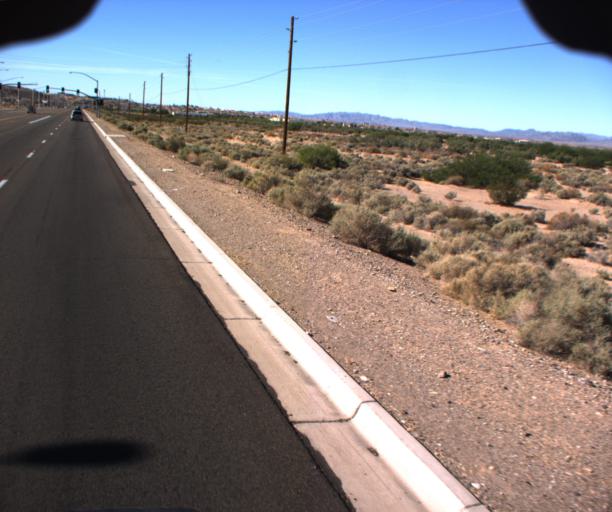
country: US
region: Arizona
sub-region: Mohave County
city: Bullhead City
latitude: 35.0639
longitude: -114.5893
